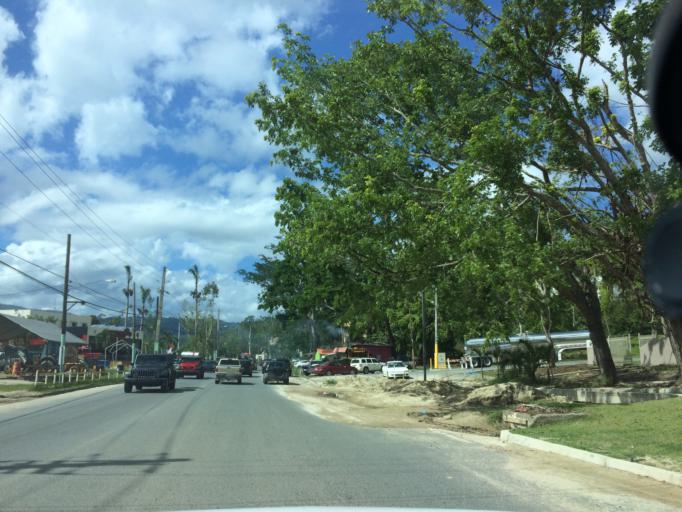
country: PR
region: Utuado
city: Utuado
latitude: 18.2690
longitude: -66.7009
